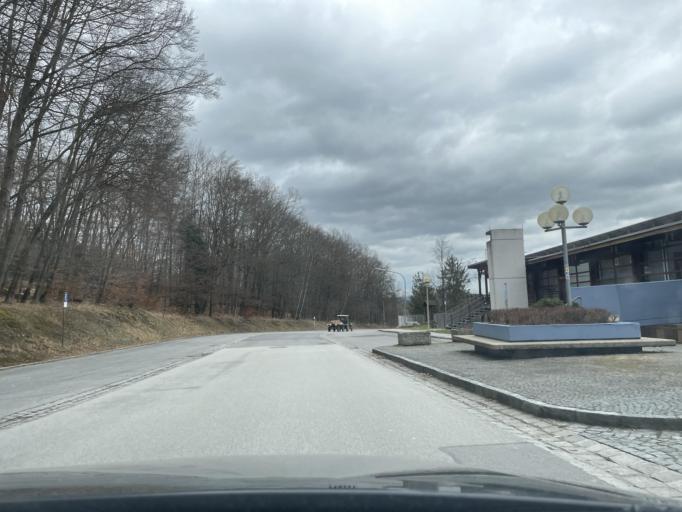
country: DE
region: Bavaria
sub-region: Lower Bavaria
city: Viechtach
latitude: 49.0806
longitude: 12.8619
